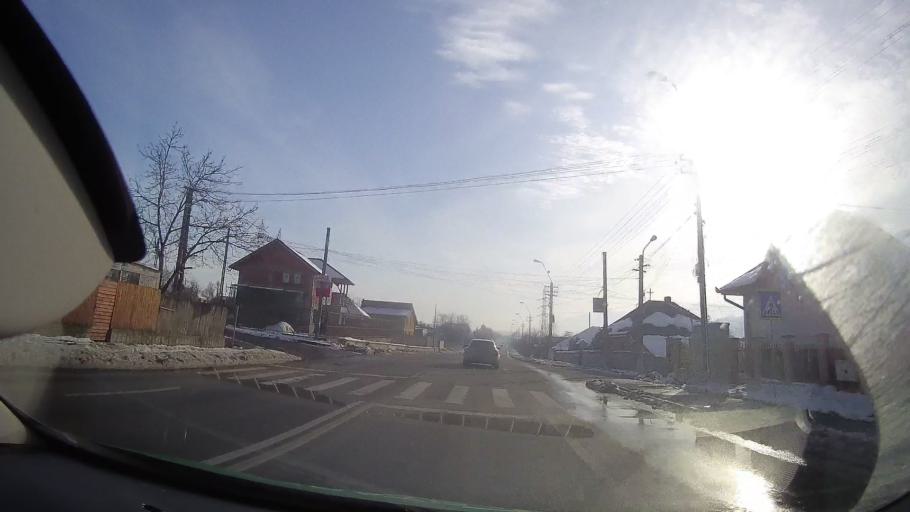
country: RO
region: Neamt
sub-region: Comuna Garcina
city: Garcina
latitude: 46.9568
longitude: 26.3831
